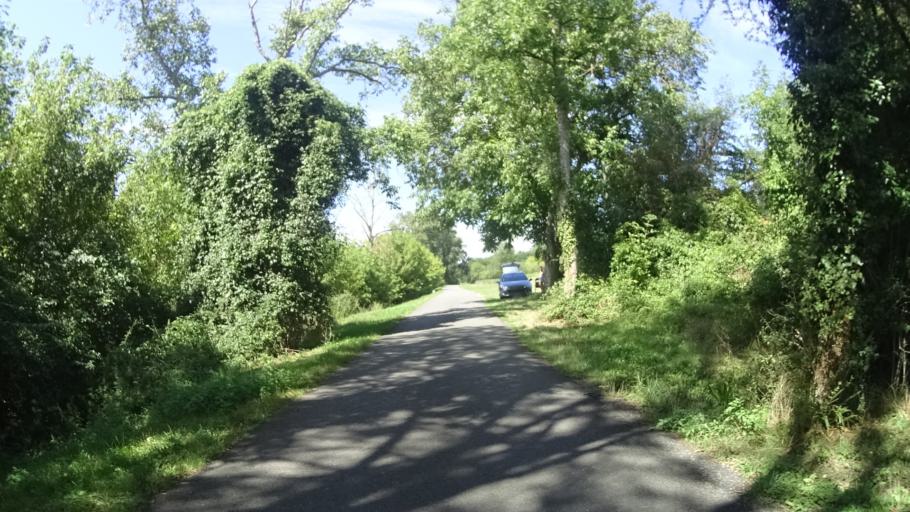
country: FR
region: Centre
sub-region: Departement du Loiret
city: Bonny-sur-Loire
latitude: 47.5809
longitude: 2.8063
